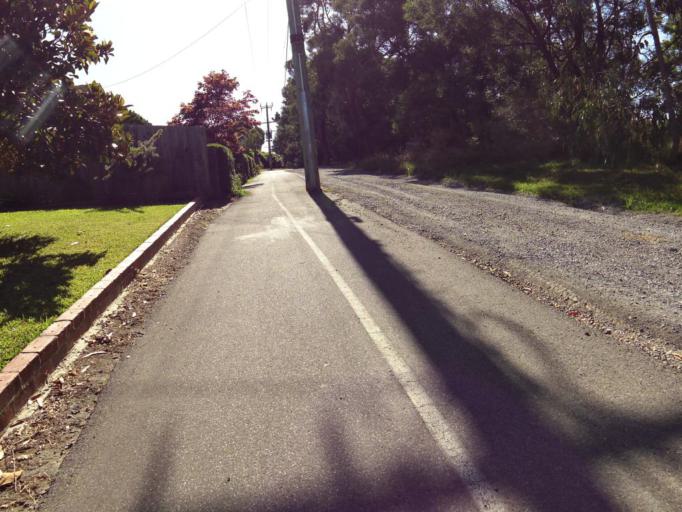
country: AU
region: Victoria
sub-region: Yarra Ranges
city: Kilsyth
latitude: -37.8010
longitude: 145.3335
